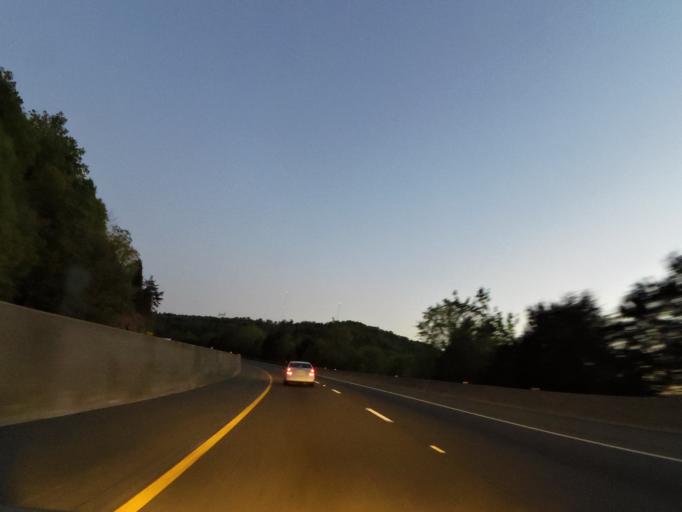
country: US
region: Tennessee
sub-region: Anderson County
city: Clinton
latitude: 36.0828
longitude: -84.0184
